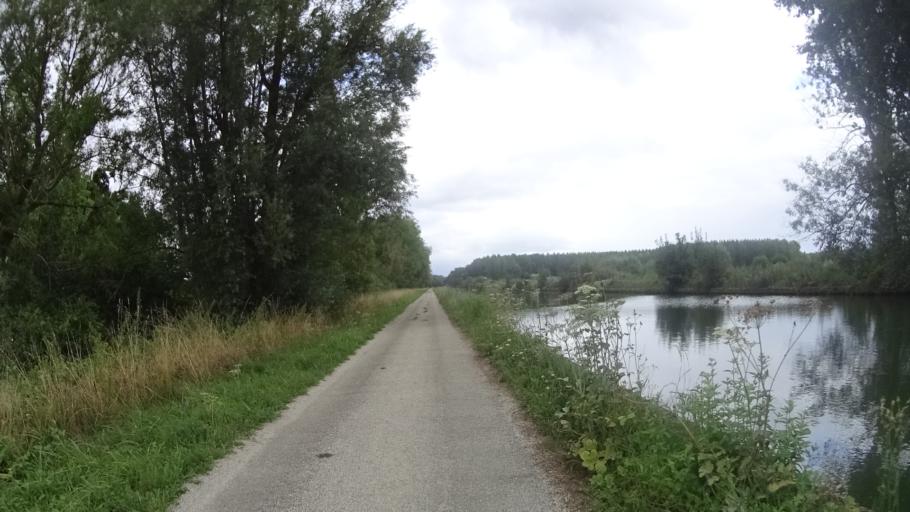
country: FR
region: Picardie
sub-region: Departement de l'Aisne
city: Ribemont
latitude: 49.7915
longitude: 3.4260
